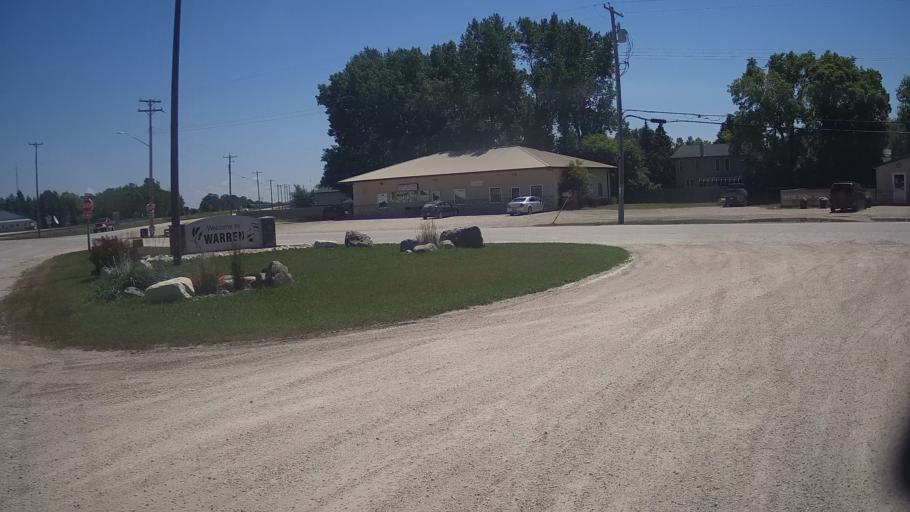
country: CA
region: Manitoba
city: Stonewall
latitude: 50.1306
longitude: -97.5450
